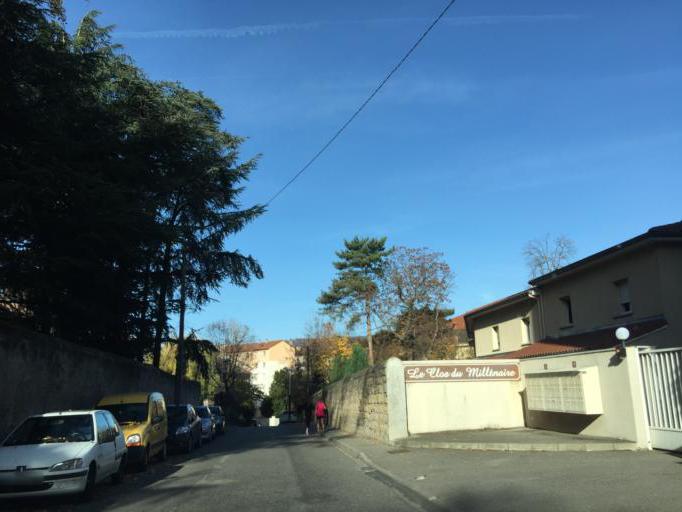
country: FR
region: Rhone-Alpes
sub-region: Departement de la Loire
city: Saint-Chamond
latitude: 45.4758
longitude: 4.5187
